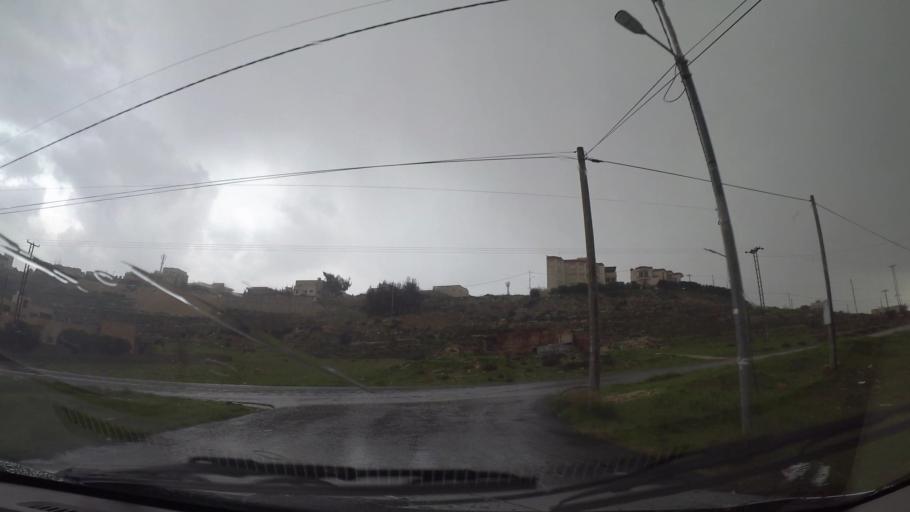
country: JO
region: Amman
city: Umm as Summaq
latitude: 31.8773
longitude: 35.8634
